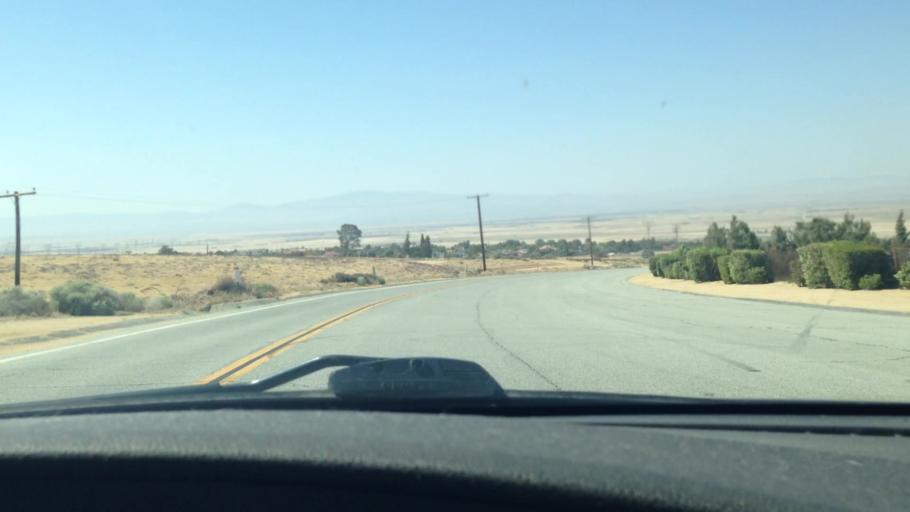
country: US
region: California
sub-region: Los Angeles County
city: Quartz Hill
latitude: 34.6347
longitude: -118.2531
